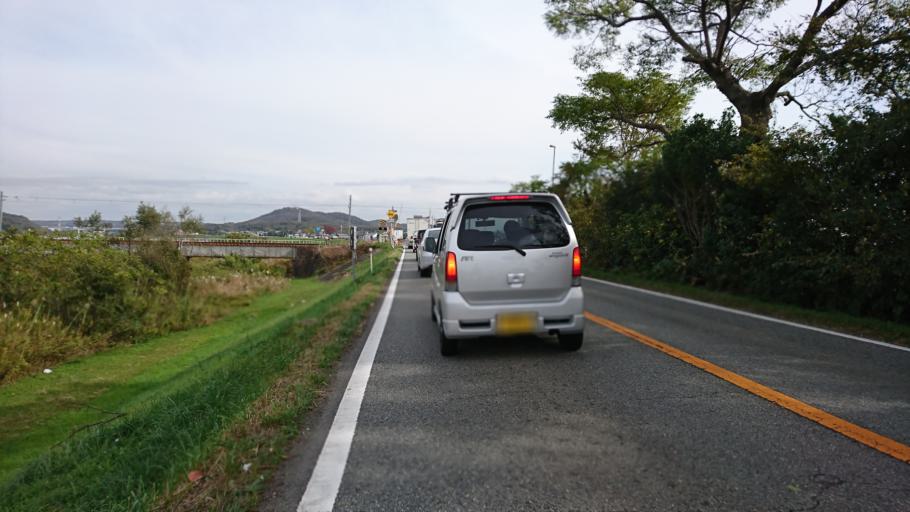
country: JP
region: Hyogo
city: Ono
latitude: 34.7976
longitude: 134.9090
